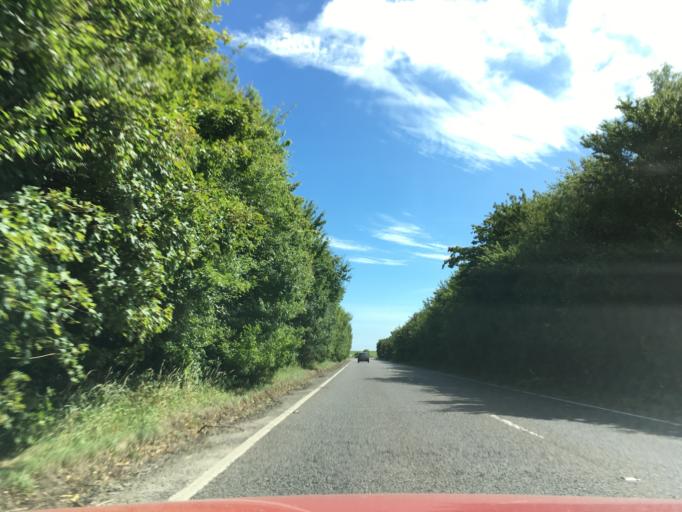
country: GB
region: England
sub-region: Dorset
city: Dorchester
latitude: 50.7754
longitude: -2.5392
